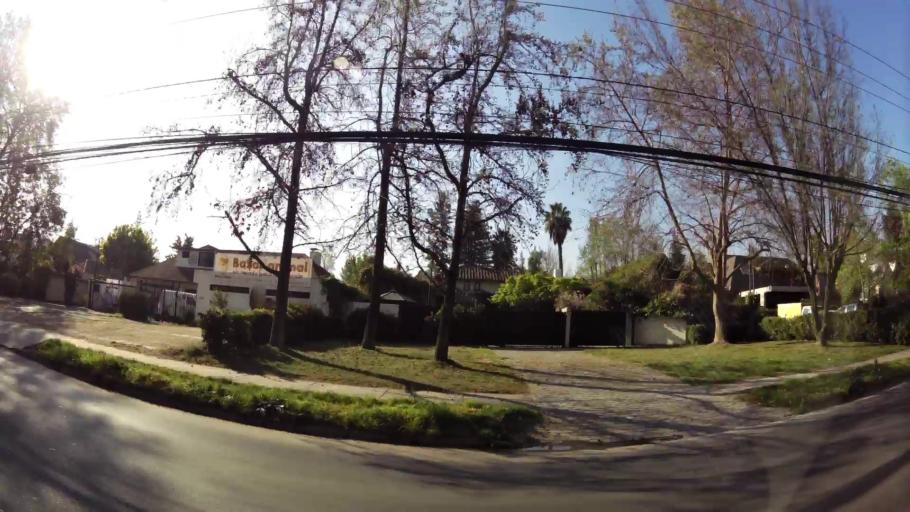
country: CL
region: Santiago Metropolitan
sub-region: Provincia de Santiago
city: Villa Presidente Frei, Nunoa, Santiago, Chile
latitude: -33.3522
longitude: -70.5148
